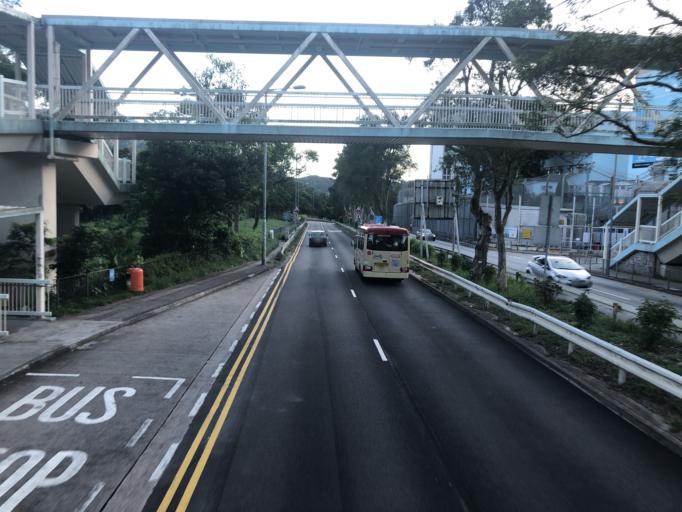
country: HK
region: Sai Kung
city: Sai Kung
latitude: 22.3395
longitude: 114.2464
